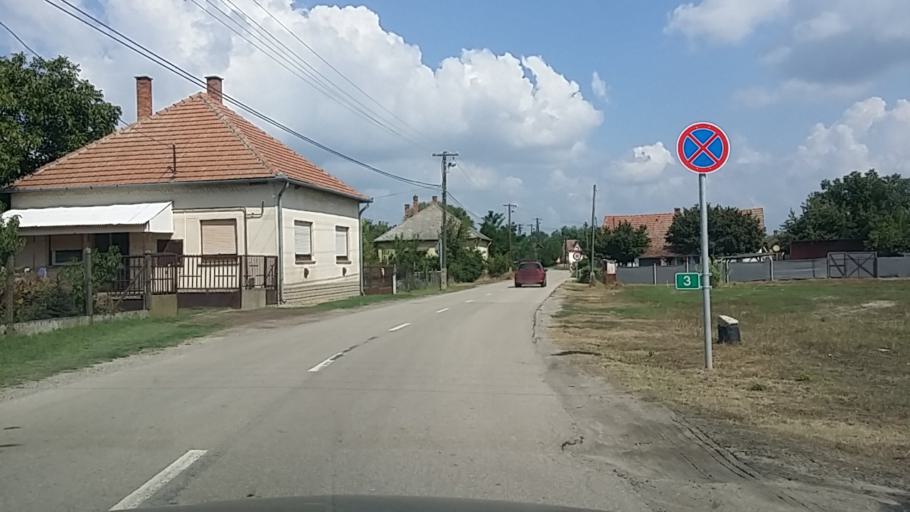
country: HU
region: Bacs-Kiskun
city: Tiszaalpar
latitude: 46.7997
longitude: 20.0059
